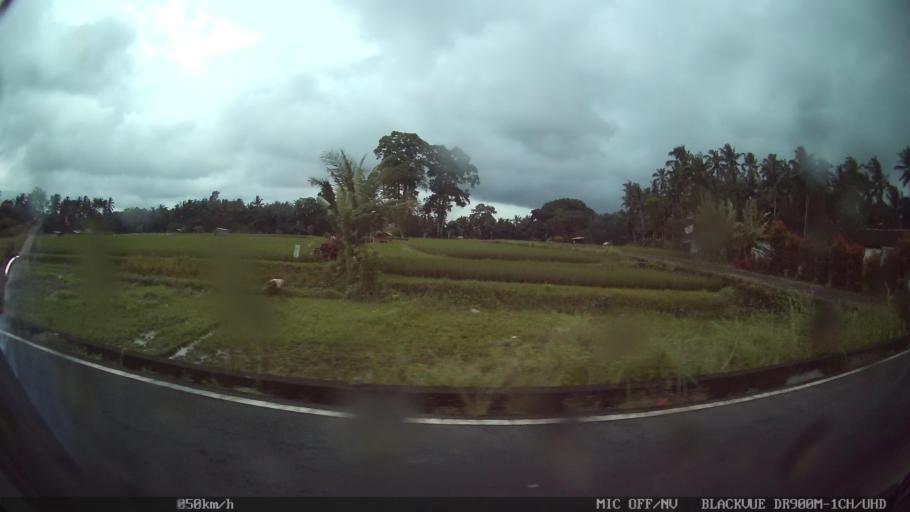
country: ID
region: Bali
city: Banjar Sayanbaleran
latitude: -8.5113
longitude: 115.1881
